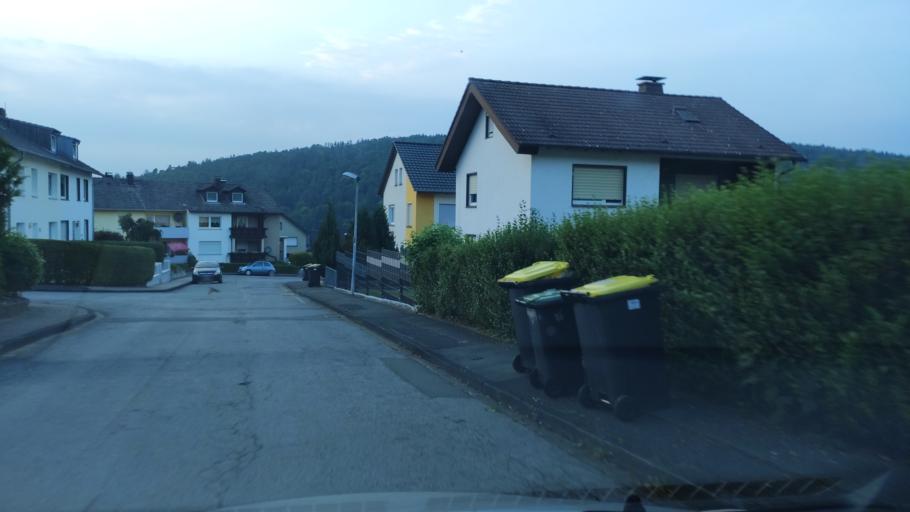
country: DE
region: North Rhine-Westphalia
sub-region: Regierungsbezirk Detmold
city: Hoexter
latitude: 51.7705
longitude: 9.3547
